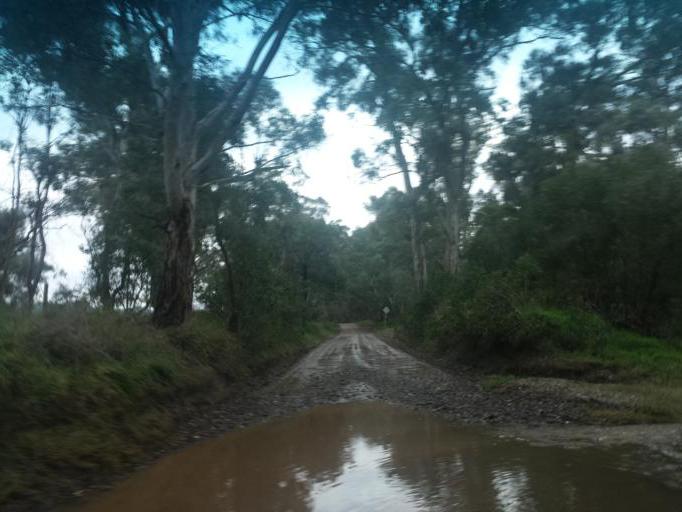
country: AU
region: Victoria
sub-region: Murrindindi
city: Kinglake West
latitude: -37.0308
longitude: 145.2044
